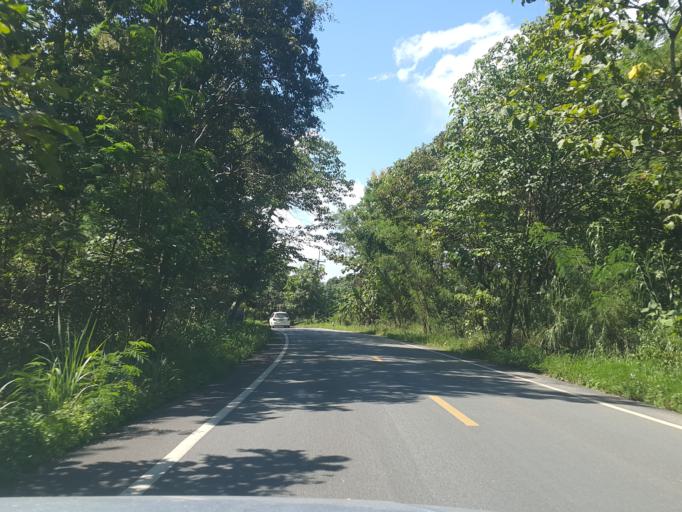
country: TH
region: Chiang Mai
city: Mae Taeng
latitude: 19.1705
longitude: 98.9274
